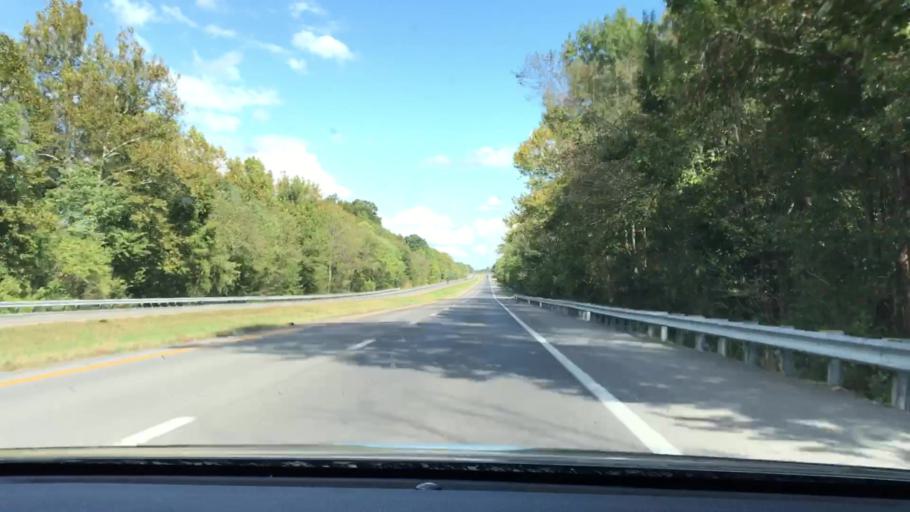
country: US
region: Kentucky
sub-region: Marshall County
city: Benton
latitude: 36.8328
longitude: -88.4408
